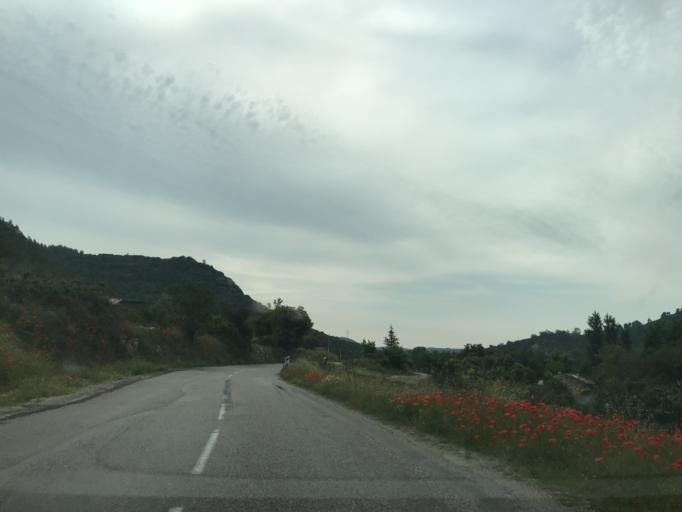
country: FR
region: Provence-Alpes-Cote d'Azur
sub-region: Departement du Vaucluse
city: Beaumont-de-Pertuis
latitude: 43.6816
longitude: 5.7165
